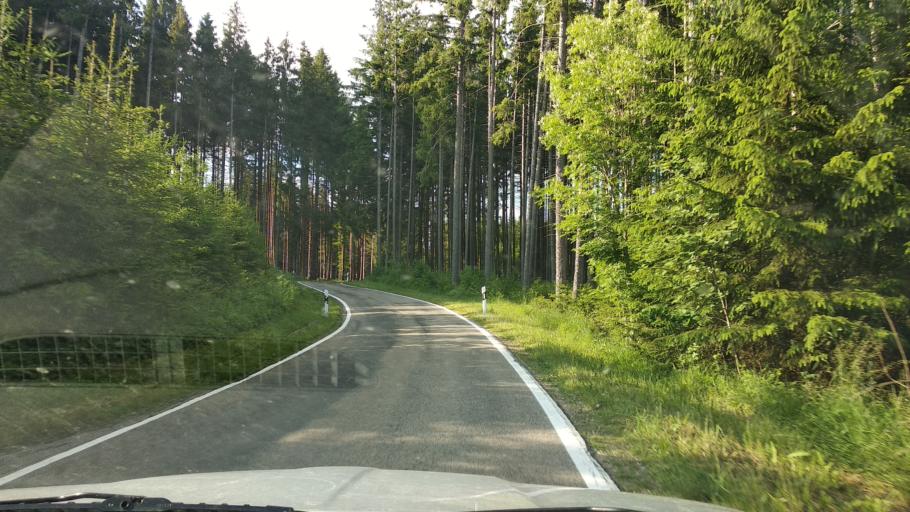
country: DE
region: Baden-Wuerttemberg
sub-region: Tuebingen Region
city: Aitrach
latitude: 47.9539
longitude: 10.0421
